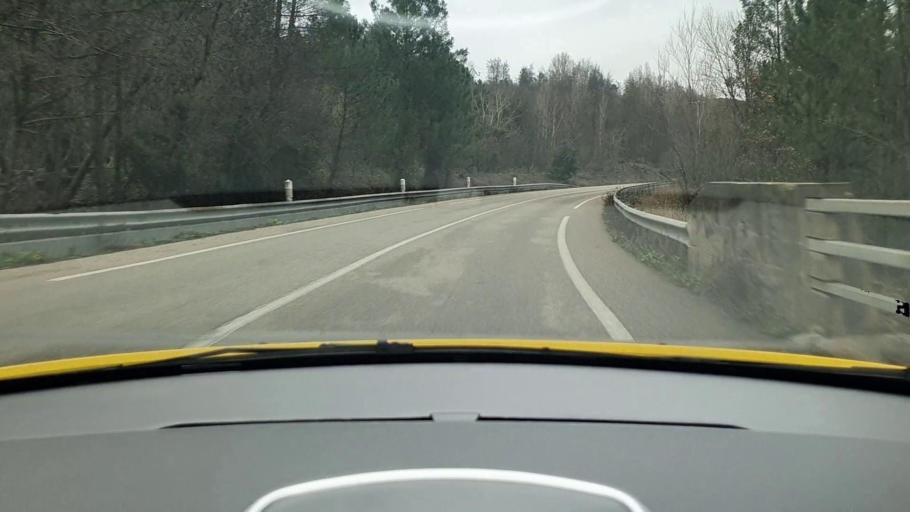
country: FR
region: Languedoc-Roussillon
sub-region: Departement du Gard
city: Laval-Pradel
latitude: 44.2224
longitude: 4.0841
